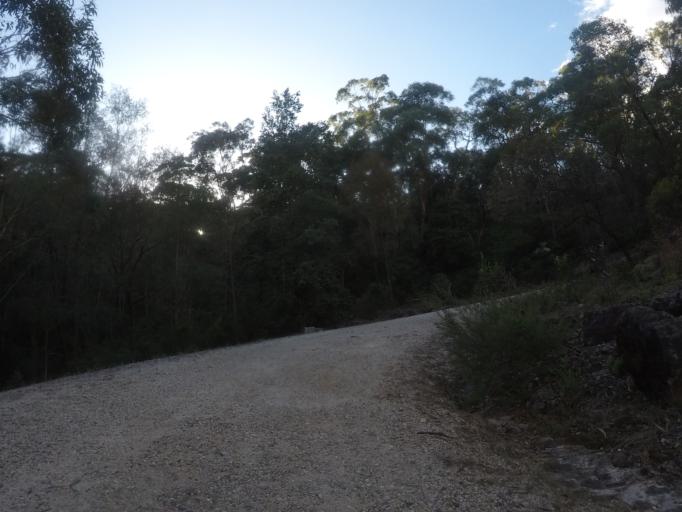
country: AU
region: New South Wales
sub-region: Hornsby Shire
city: Glenorie
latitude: -33.3660
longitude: 150.9872
